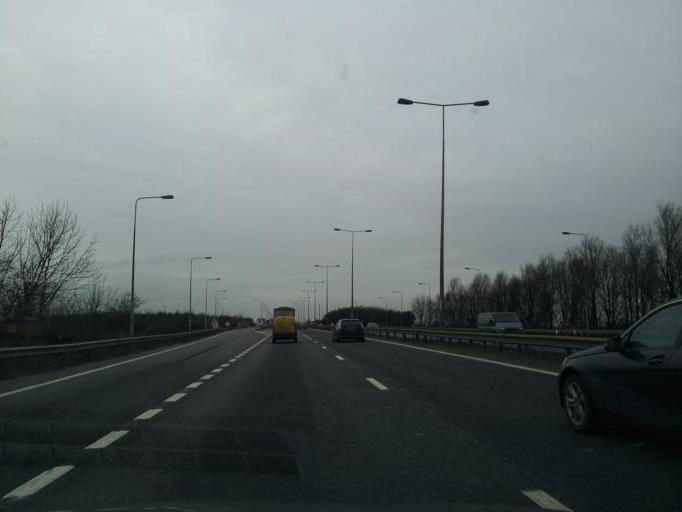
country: GB
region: England
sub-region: Cambridgeshire
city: Girton
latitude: 52.2272
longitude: 0.0744
